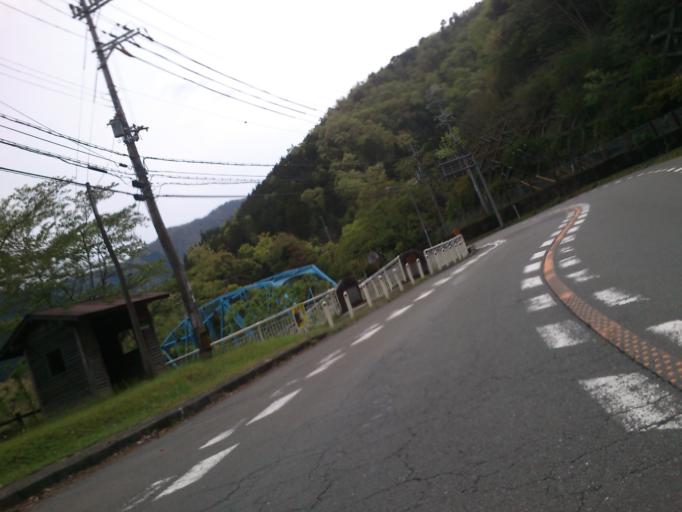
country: JP
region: Kyoto
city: Ayabe
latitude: 35.2660
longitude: 135.4842
